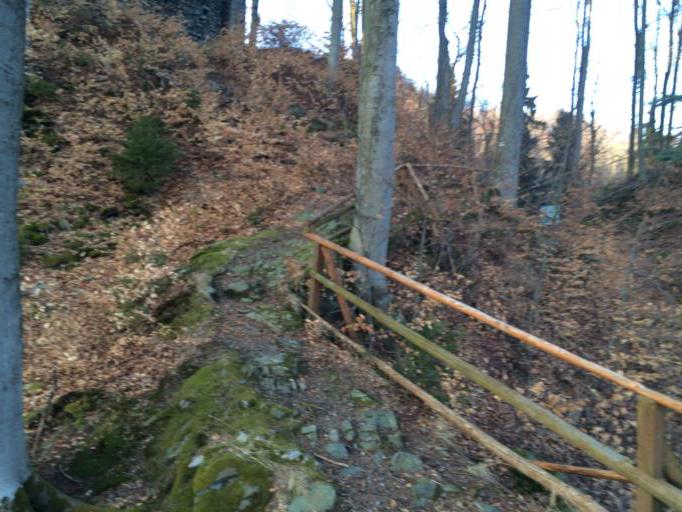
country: PL
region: Lower Silesian Voivodeship
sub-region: Powiat klodzki
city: Miedzylesie
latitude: 50.1940
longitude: 16.6205
